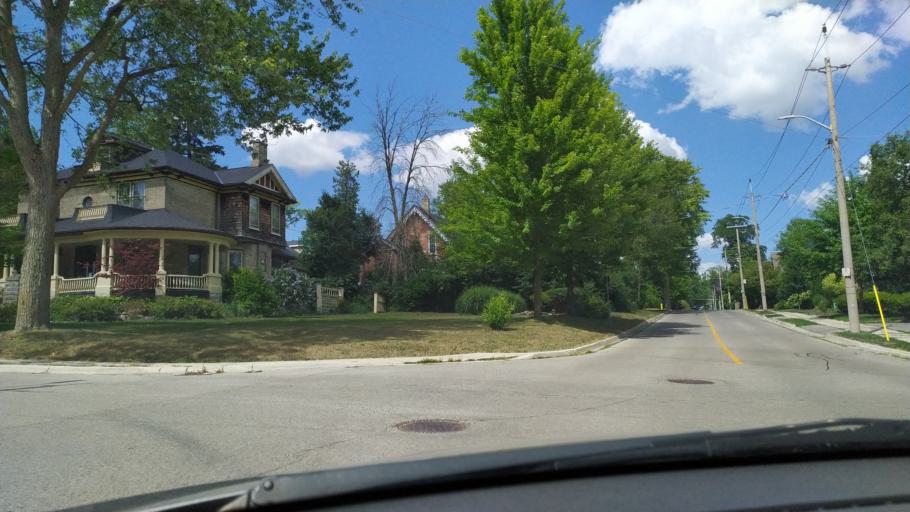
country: CA
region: Ontario
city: Stratford
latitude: 43.3725
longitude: -80.9896
